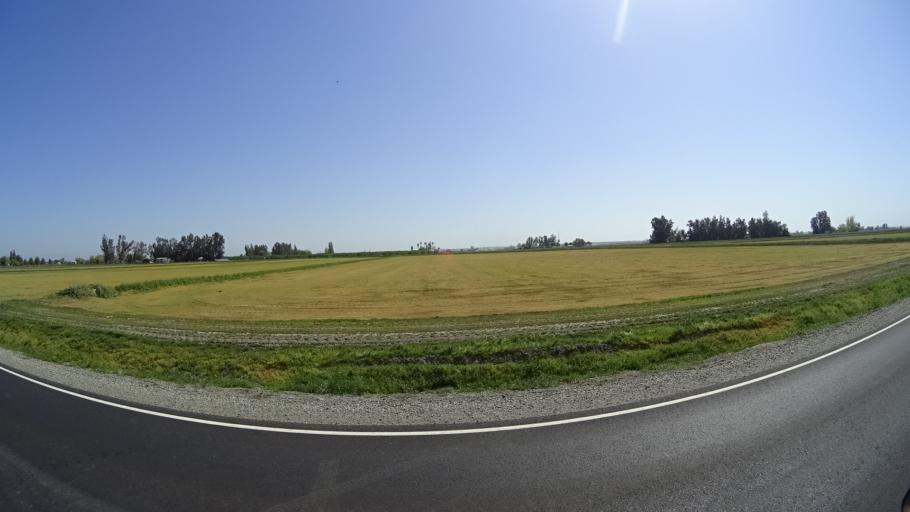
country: US
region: California
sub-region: Glenn County
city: Willows
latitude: 39.5982
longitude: -122.0652
